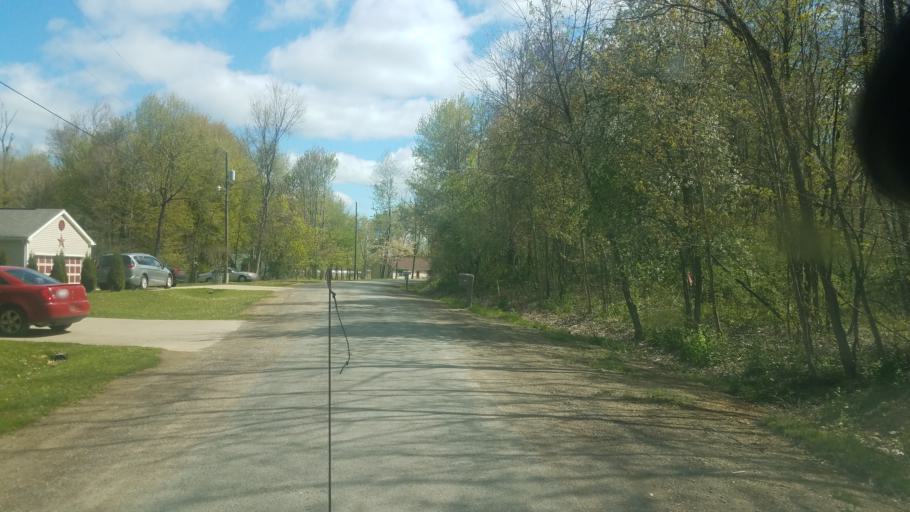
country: US
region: Ohio
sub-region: Knox County
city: Danville
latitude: 40.4645
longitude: -82.3302
